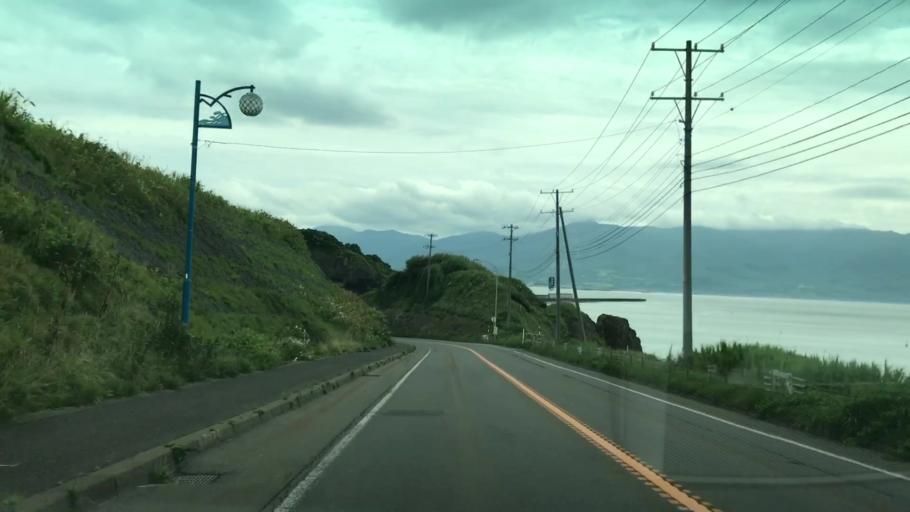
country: JP
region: Hokkaido
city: Iwanai
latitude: 43.0469
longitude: 140.5045
